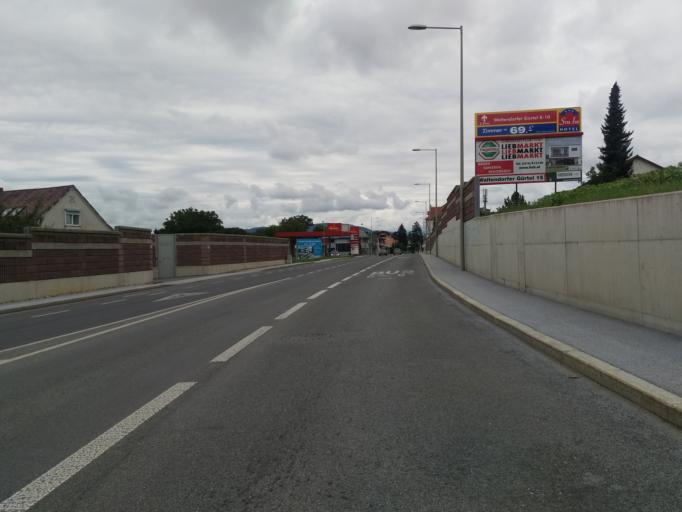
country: AT
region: Styria
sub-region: Politischer Bezirk Graz-Umgebung
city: Raaba
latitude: 47.0489
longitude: 15.4822
